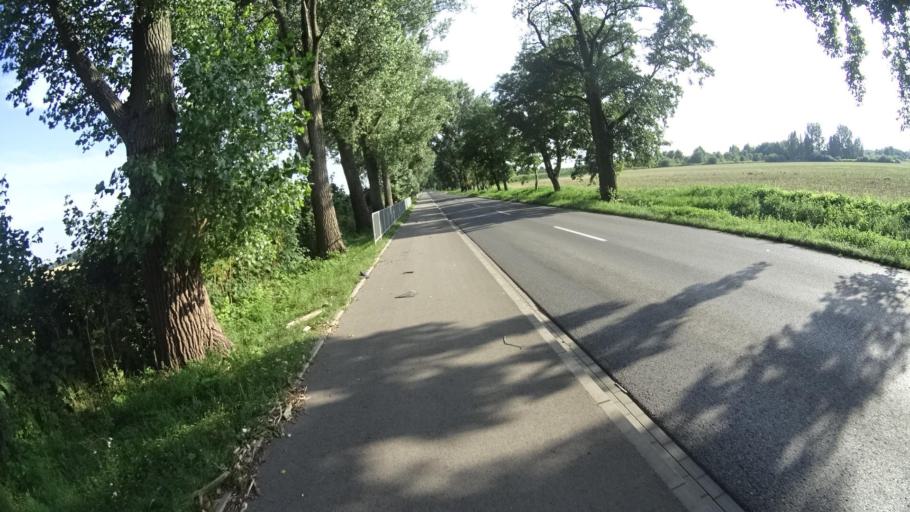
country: PL
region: Masovian Voivodeship
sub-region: Powiat pruszkowski
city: Nadarzyn
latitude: 52.0581
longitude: 20.7857
